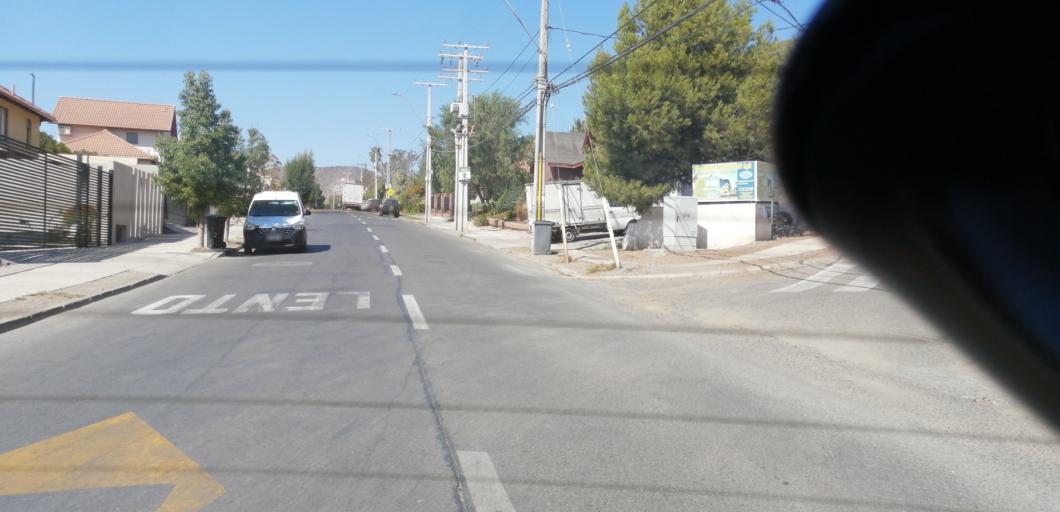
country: CL
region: Santiago Metropolitan
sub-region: Provincia de Santiago
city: Lo Prado
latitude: -33.4516
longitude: -70.8237
